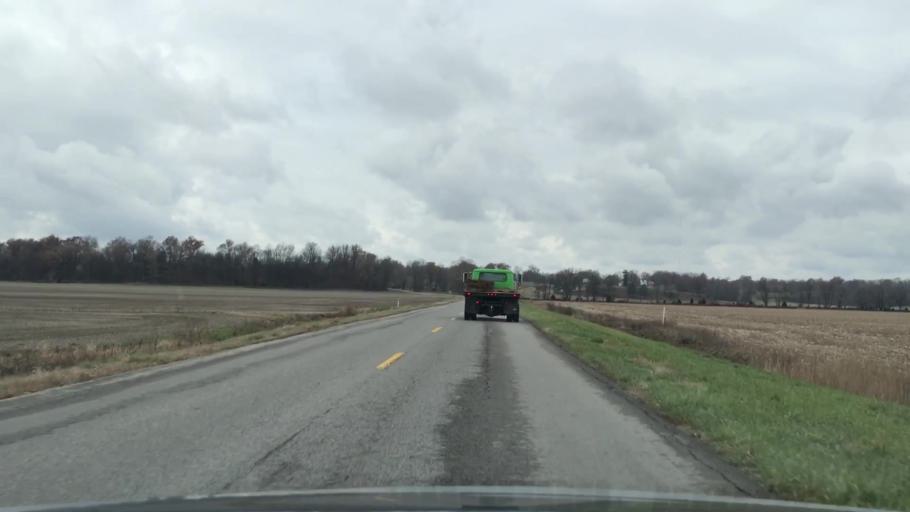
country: US
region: Kentucky
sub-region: McLean County
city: Calhoun
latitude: 37.5230
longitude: -87.3795
